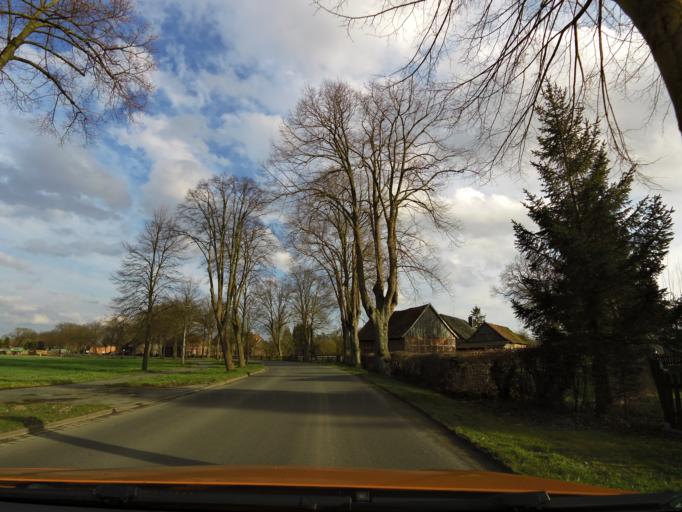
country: DE
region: Lower Saxony
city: Grethem
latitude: 52.7023
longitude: 9.5469
